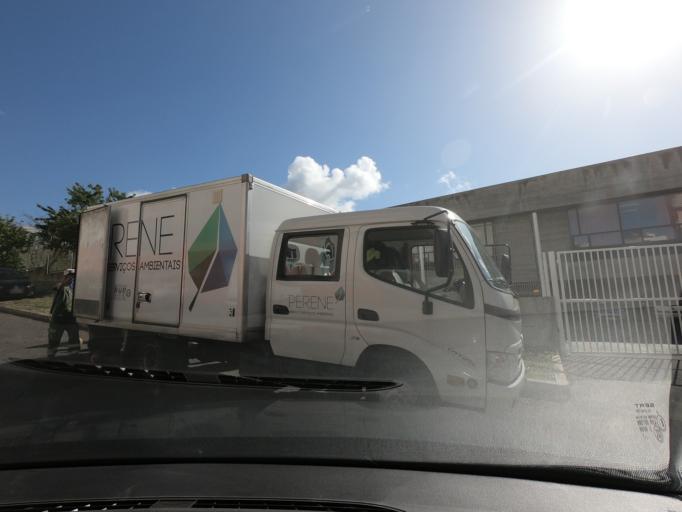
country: PT
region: Lisbon
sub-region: Oeiras
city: Paco de Arcos
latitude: 38.6987
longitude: -9.2998
